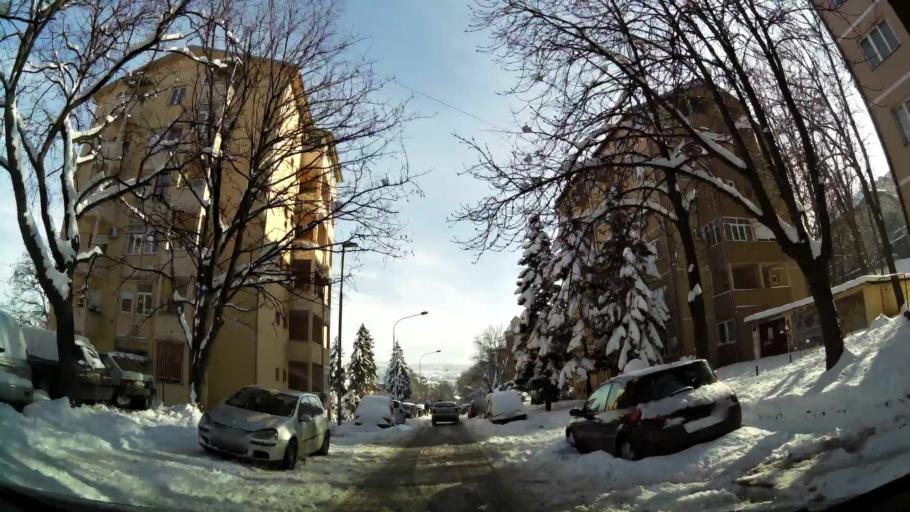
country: RS
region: Central Serbia
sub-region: Belgrade
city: Palilula
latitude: 44.8077
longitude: 20.5202
